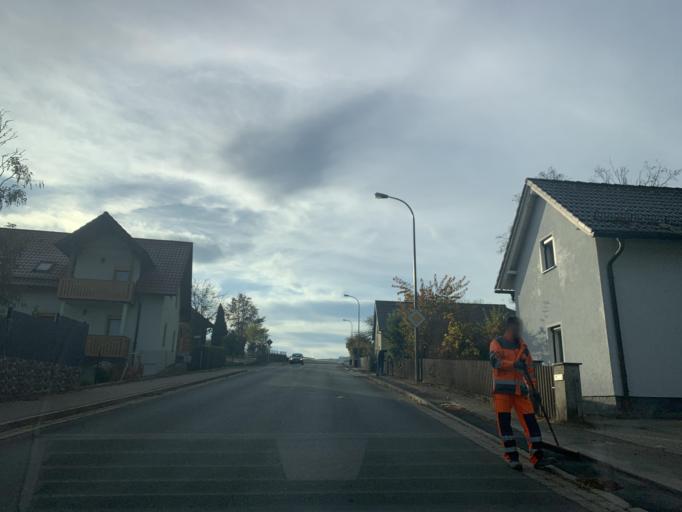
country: DE
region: Bavaria
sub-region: Upper Palatinate
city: Neunburg vorm Wald
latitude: 49.3432
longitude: 12.3915
